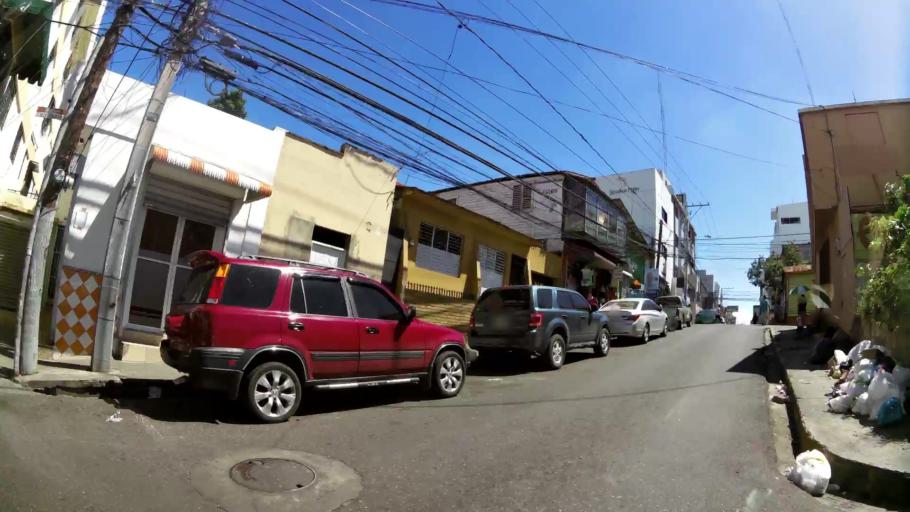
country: DO
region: Santiago
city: Santiago de los Caballeros
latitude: 19.4537
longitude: -70.7008
